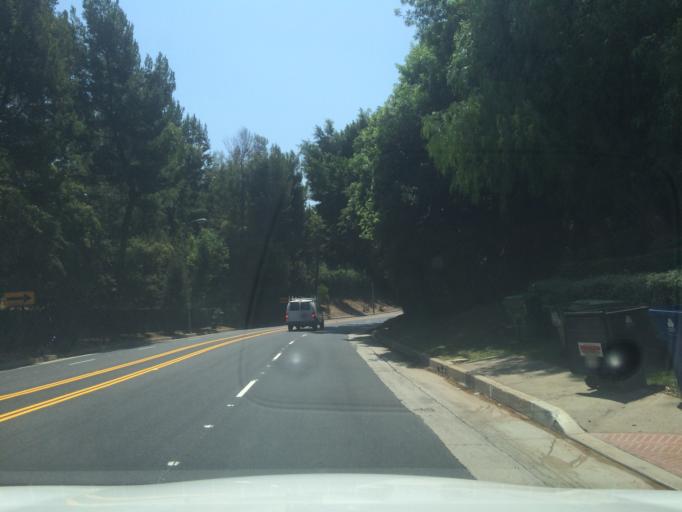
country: US
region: California
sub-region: Los Angeles County
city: Westwood, Los Angeles
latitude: 34.0818
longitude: -118.4315
